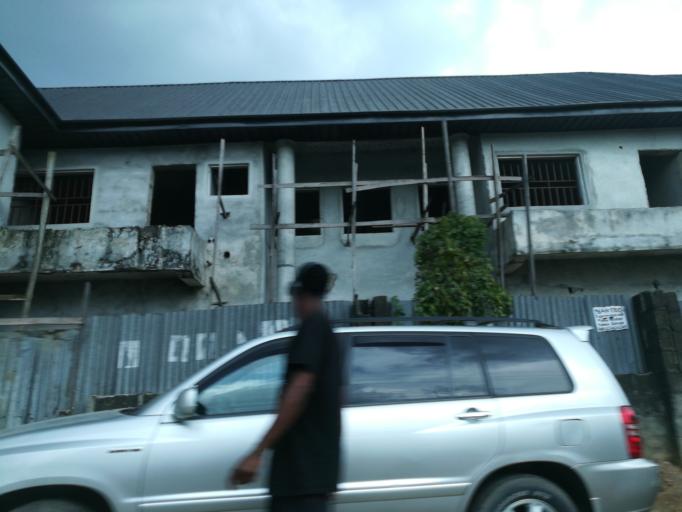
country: NG
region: Rivers
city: Port Harcourt
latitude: 4.8184
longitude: 7.0672
